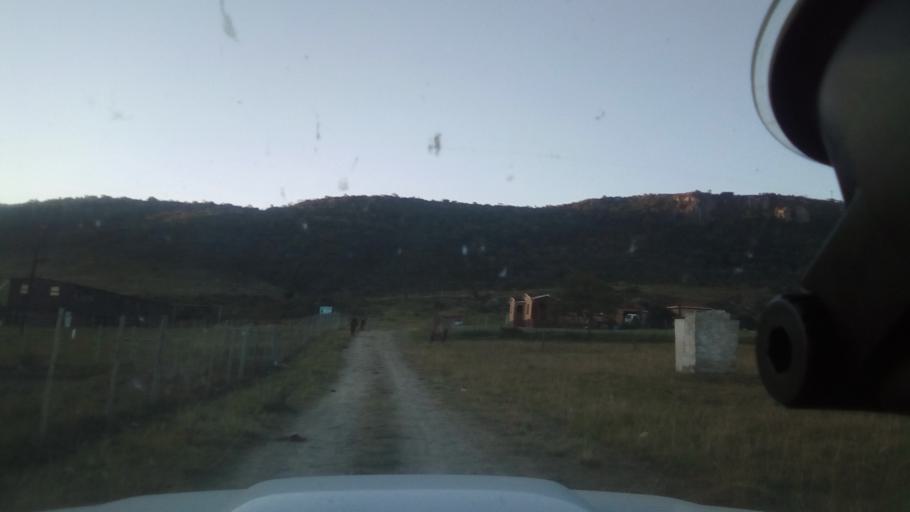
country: ZA
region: Eastern Cape
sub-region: Buffalo City Metropolitan Municipality
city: Bhisho
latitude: -32.7345
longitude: 27.3732
